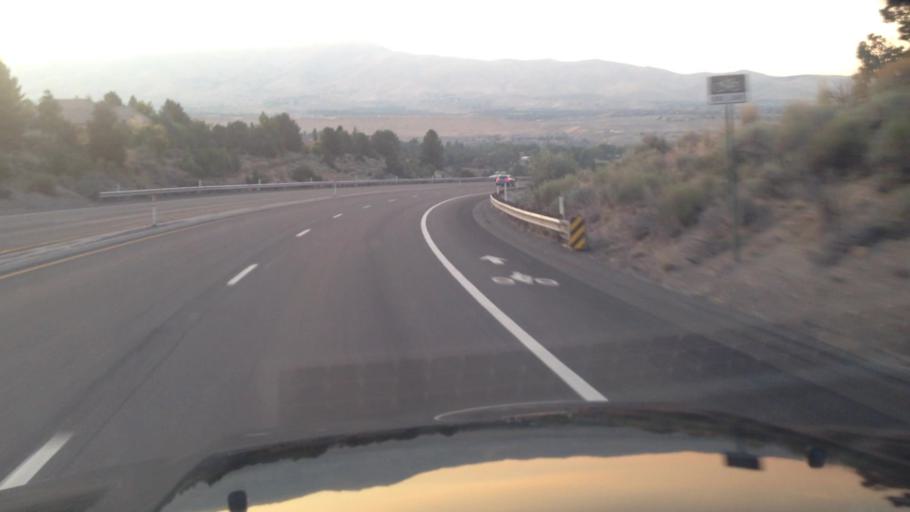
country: US
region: Nevada
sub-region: Washoe County
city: Reno
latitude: 39.4870
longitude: -119.8646
